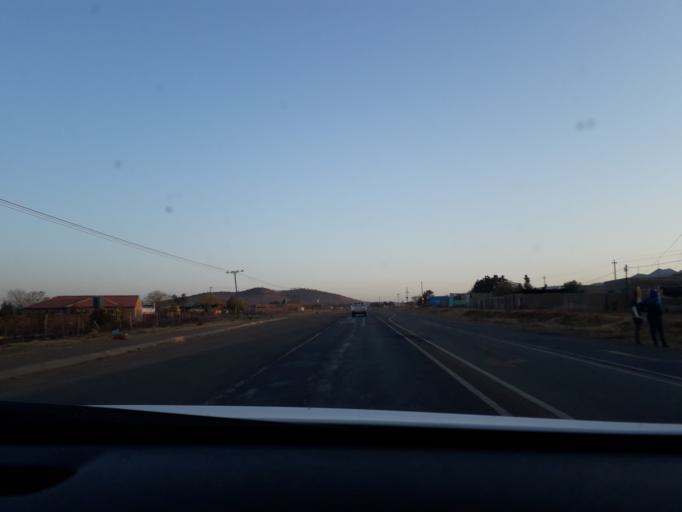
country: ZA
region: Limpopo
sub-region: Waterberg District Municipality
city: Mokopane
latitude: -24.0789
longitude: 28.9710
